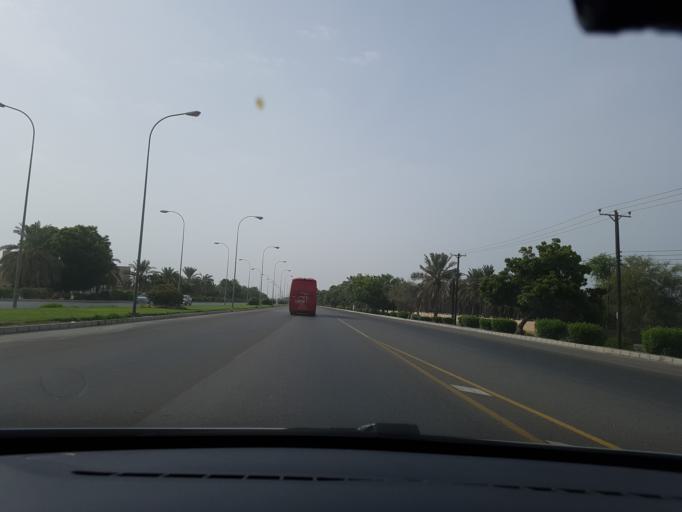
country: OM
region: Al Batinah
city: Al Sohar
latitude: 24.3701
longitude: 56.7052
